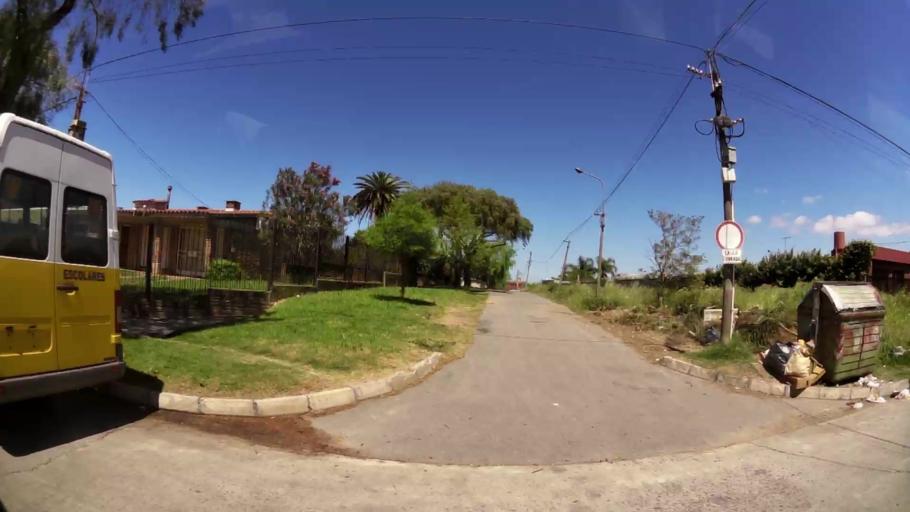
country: UY
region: Canelones
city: Paso de Carrasco
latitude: -34.8831
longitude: -56.0988
